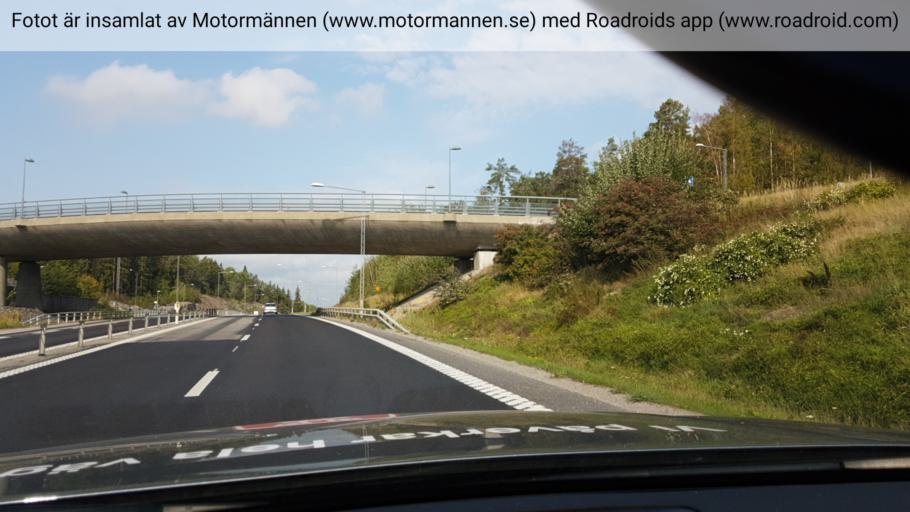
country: SE
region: Stockholm
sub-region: Botkyrka Kommun
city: Tumba
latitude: 59.2093
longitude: 17.8356
